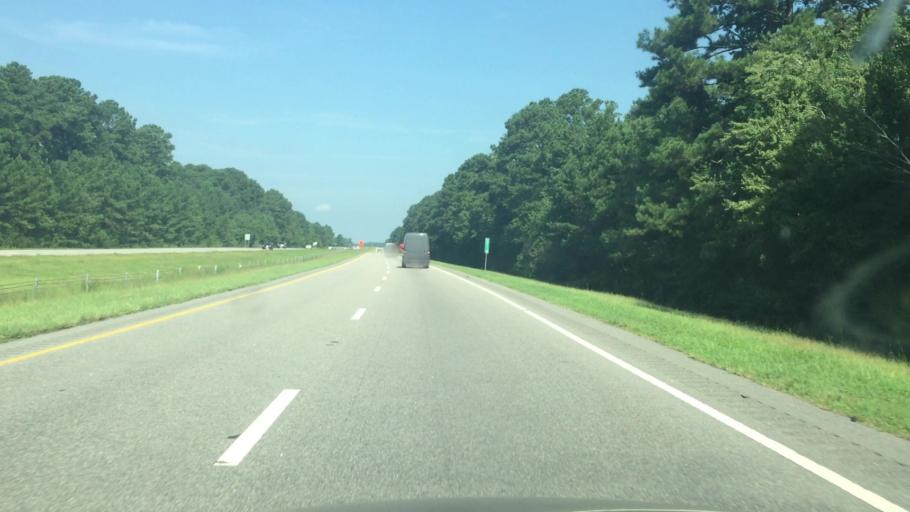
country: US
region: North Carolina
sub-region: Robeson County
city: Lumberton
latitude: 34.5729
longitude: -79.0351
